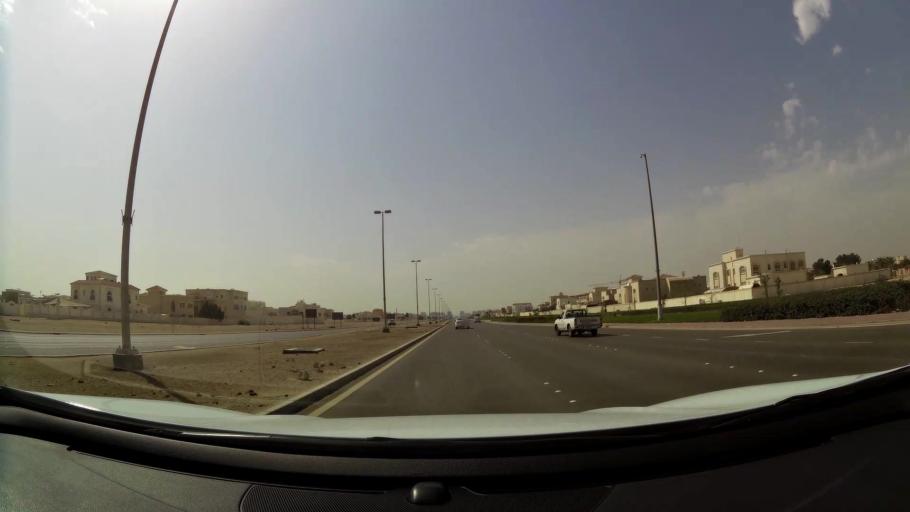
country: AE
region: Abu Dhabi
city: Abu Dhabi
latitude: 24.3256
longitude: 54.5609
